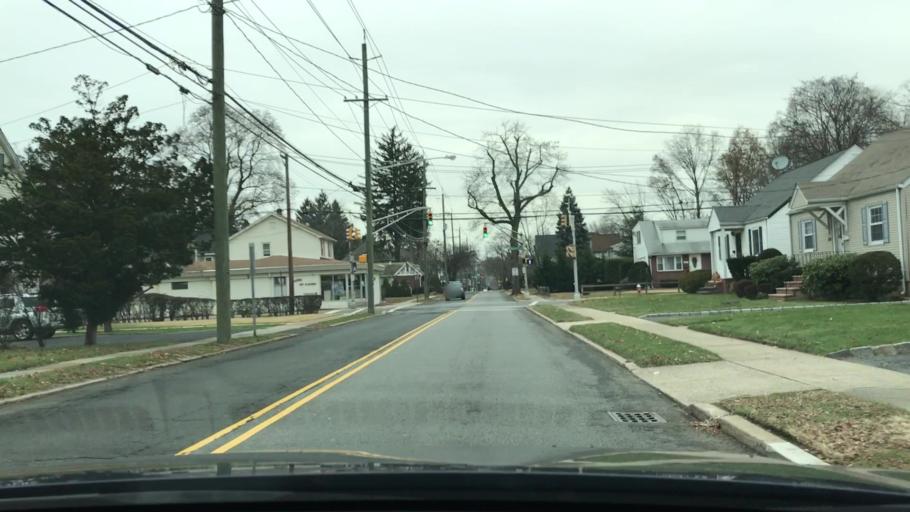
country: US
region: New Jersey
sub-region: Bergen County
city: New Milford
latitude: 40.9422
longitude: -74.0162
